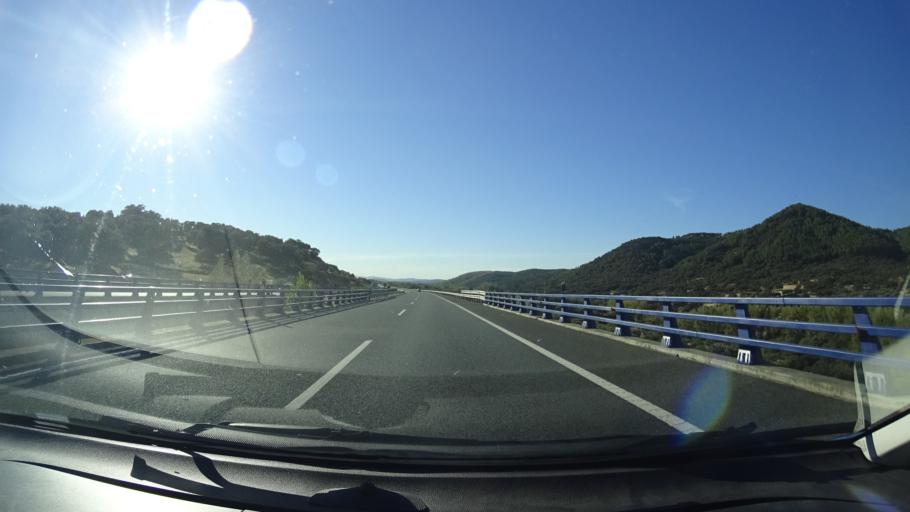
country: ES
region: Extremadura
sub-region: Provincia de Badajoz
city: Monesterio
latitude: 38.0539
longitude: -6.2384
